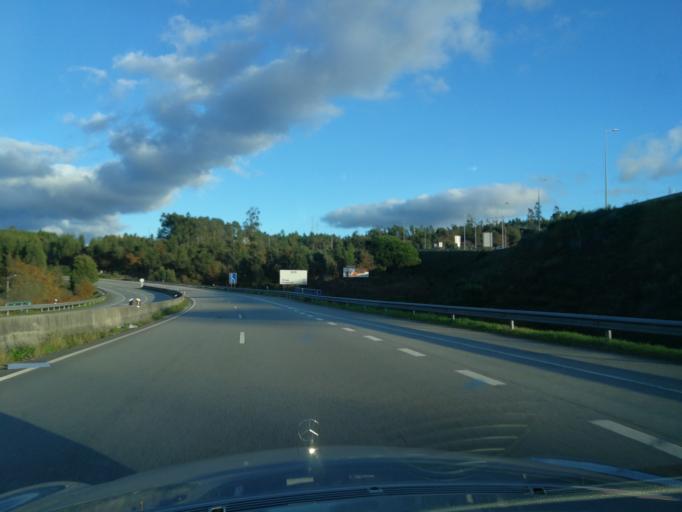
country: PT
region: Braga
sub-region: Barcelos
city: Barcelos
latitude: 41.5170
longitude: -8.6117
